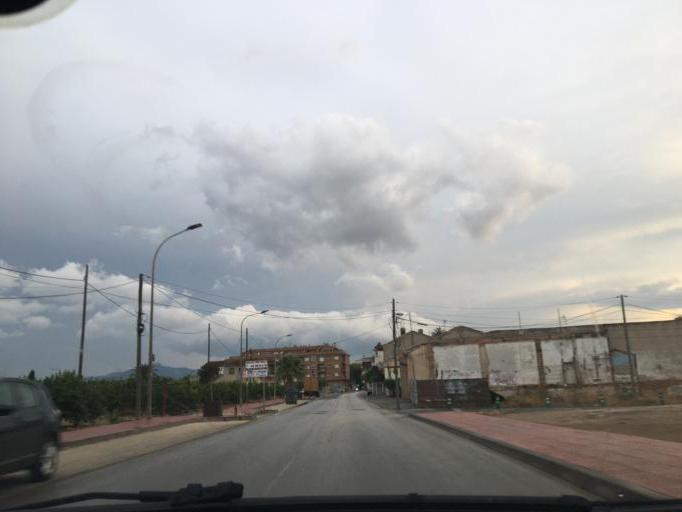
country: ES
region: Murcia
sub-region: Murcia
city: Santomera
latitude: 38.0179
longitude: -1.0509
